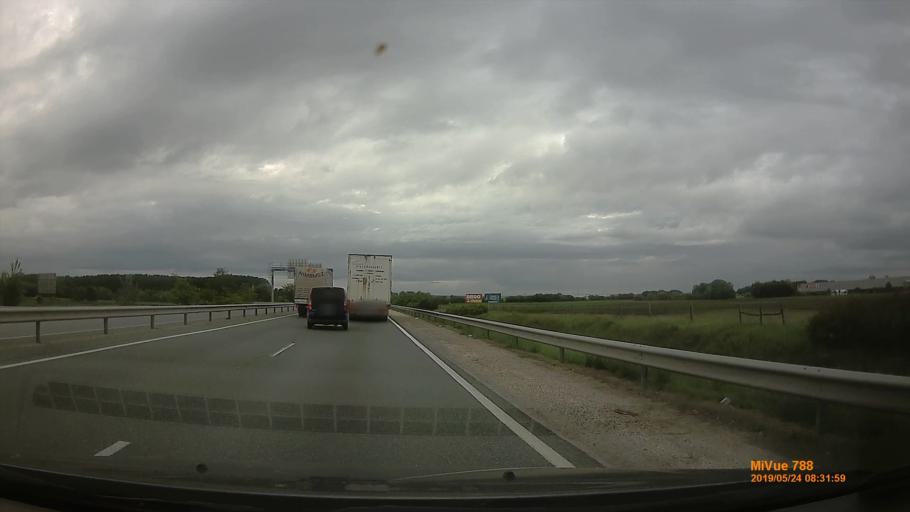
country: HU
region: Pest
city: Ullo
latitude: 47.4040
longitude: 19.3335
